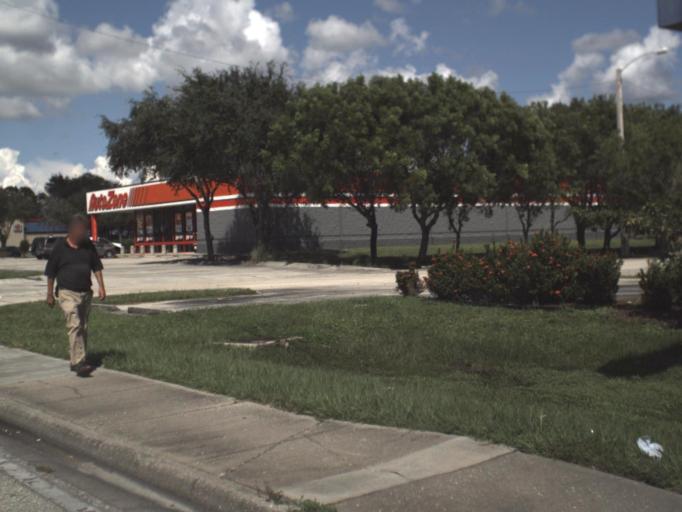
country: US
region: Florida
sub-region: Lee County
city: Lochmoor Waterway Estates
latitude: 26.6319
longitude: -81.9407
